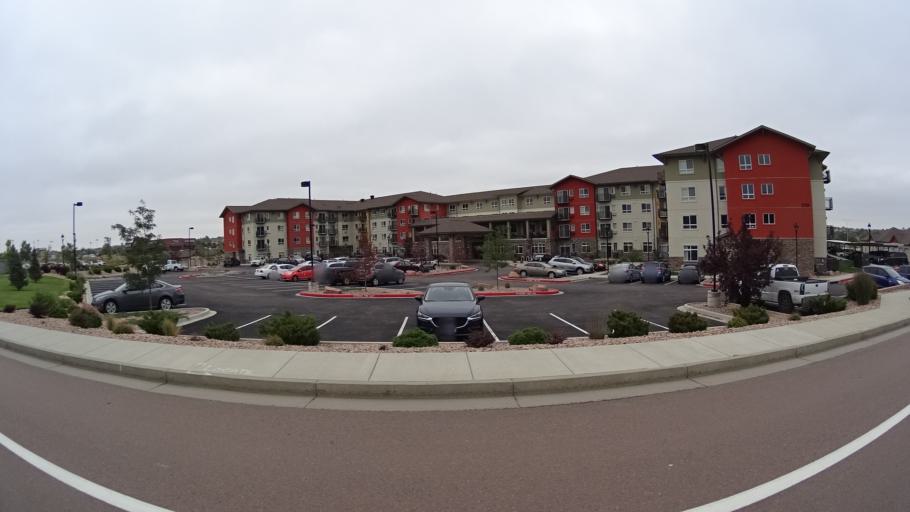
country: US
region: Colorado
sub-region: El Paso County
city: Cimarron Hills
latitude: 38.8871
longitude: -104.7137
